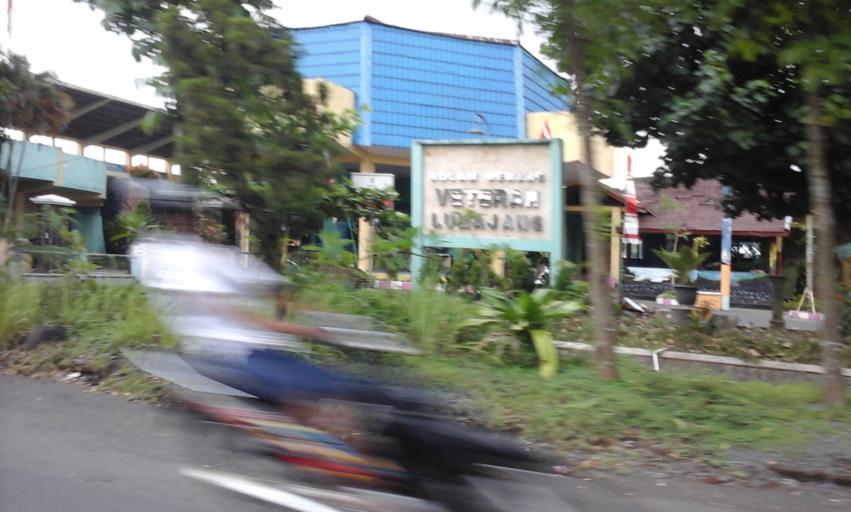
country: ID
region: East Java
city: Rogotrunan
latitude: -8.1188
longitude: 113.2205
